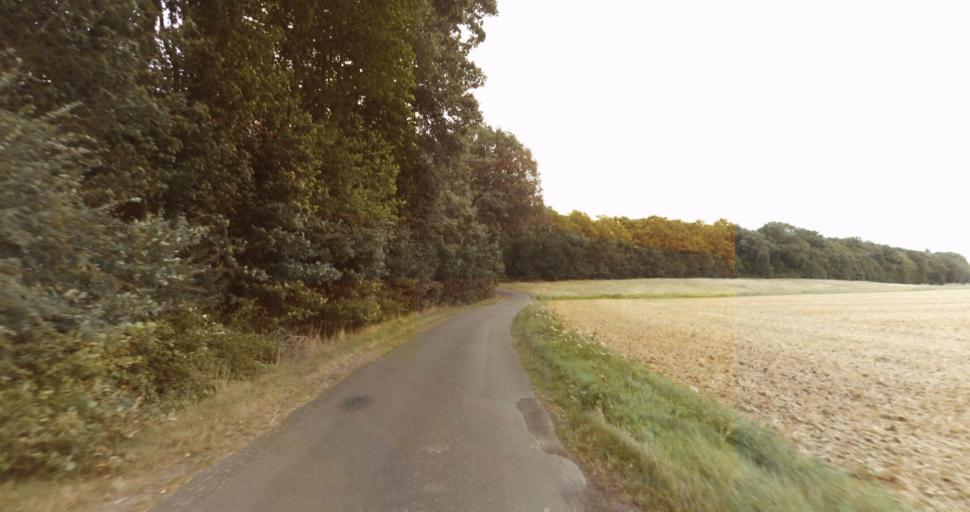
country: FR
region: Haute-Normandie
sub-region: Departement de l'Eure
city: La Couture-Boussey
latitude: 48.9027
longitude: 1.3630
